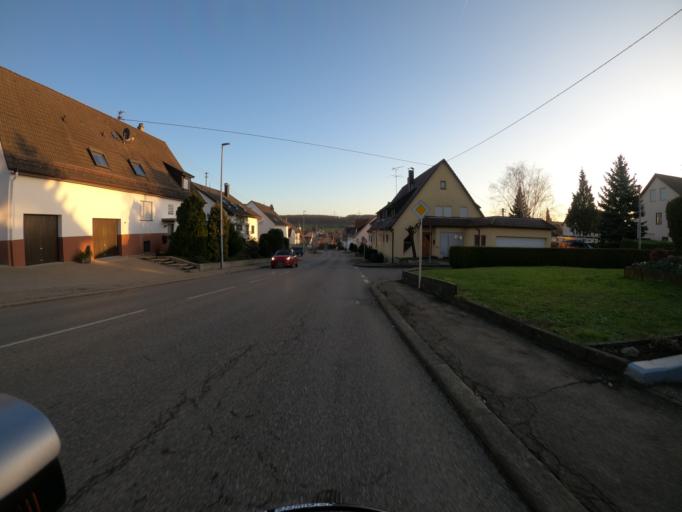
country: DE
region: Baden-Wuerttemberg
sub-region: Regierungsbezirk Stuttgart
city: Notzingen
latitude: 48.6738
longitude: 9.4544
